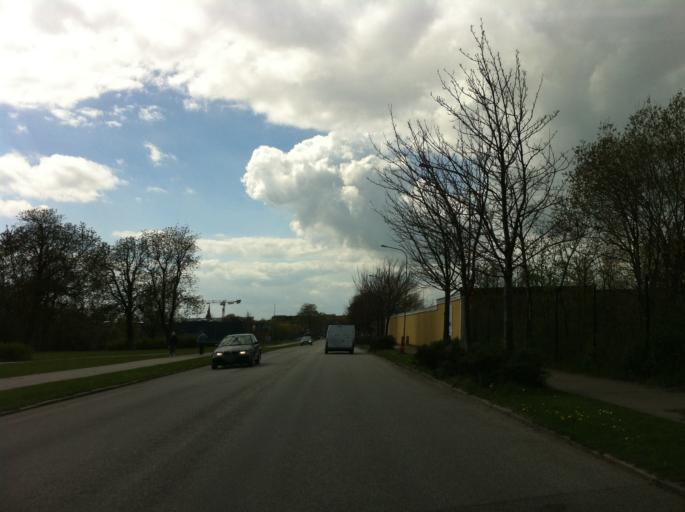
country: SE
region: Skane
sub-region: Eslovs Kommun
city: Eslov
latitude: 55.8400
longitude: 13.3158
